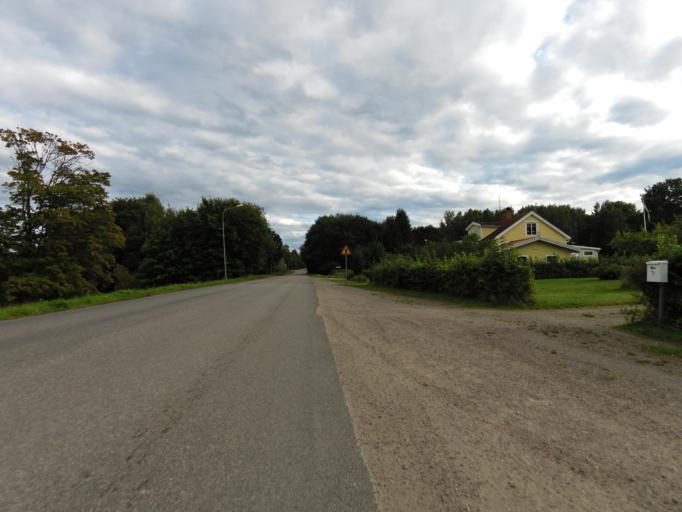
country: SE
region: Gaevleborg
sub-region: Gavle Kommun
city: Valbo
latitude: 60.6518
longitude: 17.0148
